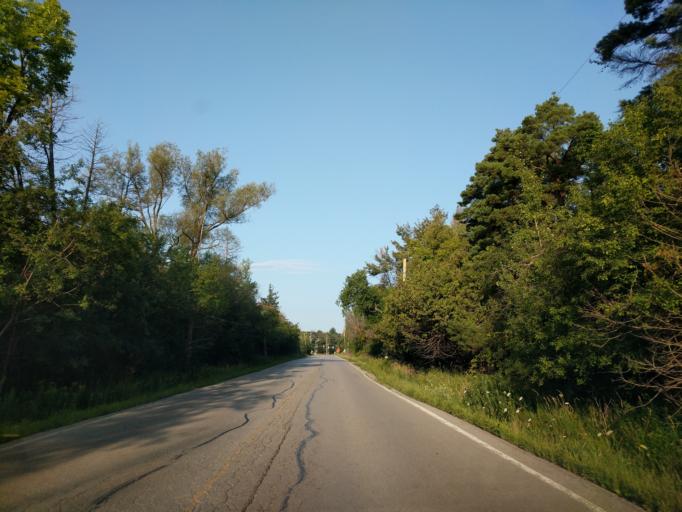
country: CA
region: Ontario
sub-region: York
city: Richmond Hill
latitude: 43.9120
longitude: -79.4196
